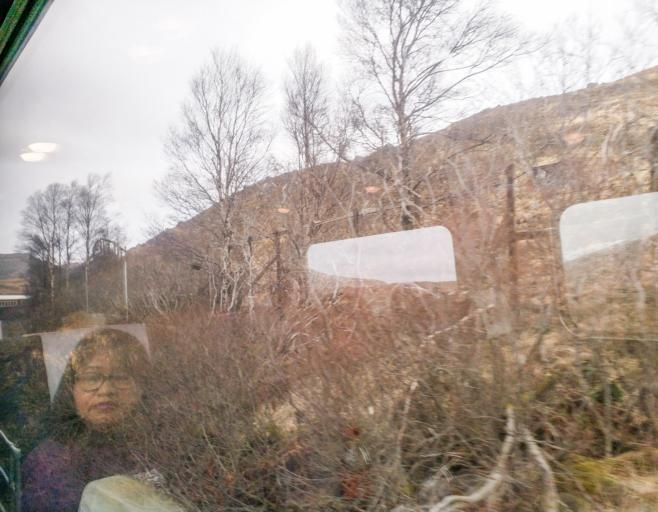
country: GB
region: Scotland
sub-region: Highland
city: Spean Bridge
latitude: 56.7748
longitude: -4.7257
